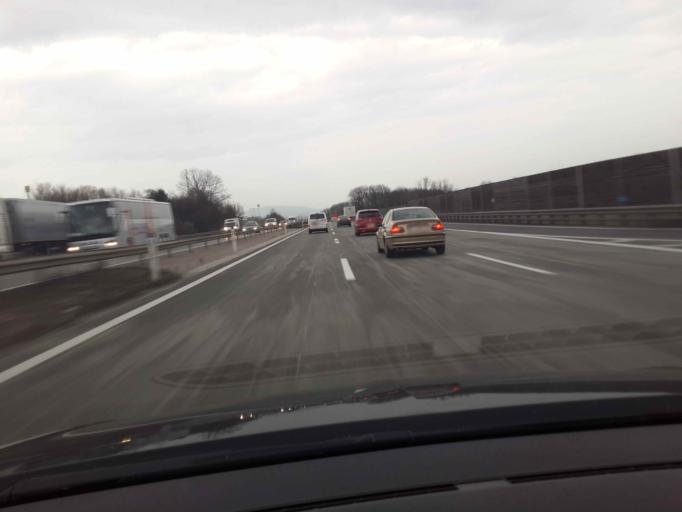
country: AT
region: Lower Austria
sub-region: Politischer Bezirk Sankt Polten
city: Gerersdorf
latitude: 48.1776
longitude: 15.5617
